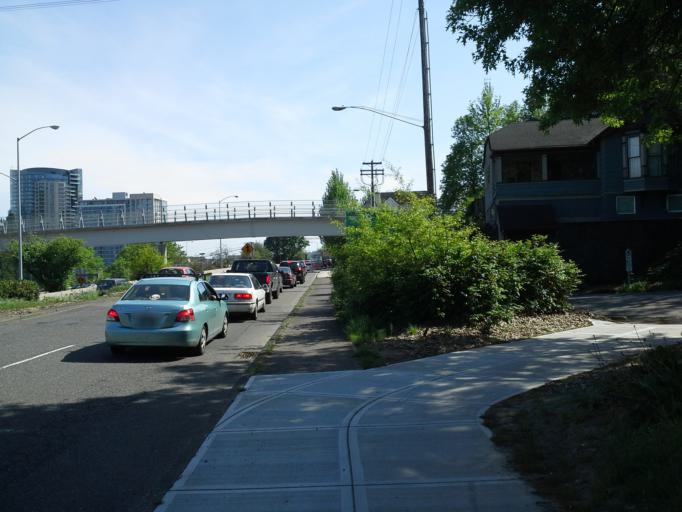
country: US
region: Oregon
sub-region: Multnomah County
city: Portland
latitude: 45.5003
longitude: -122.6743
